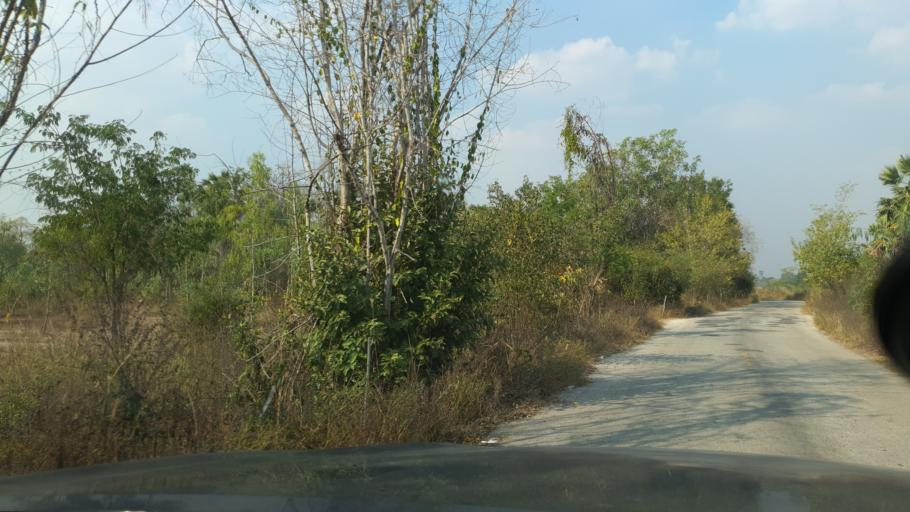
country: TH
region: Sukhothai
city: Ban Dan Lan Hoi
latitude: 17.0159
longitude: 99.5582
